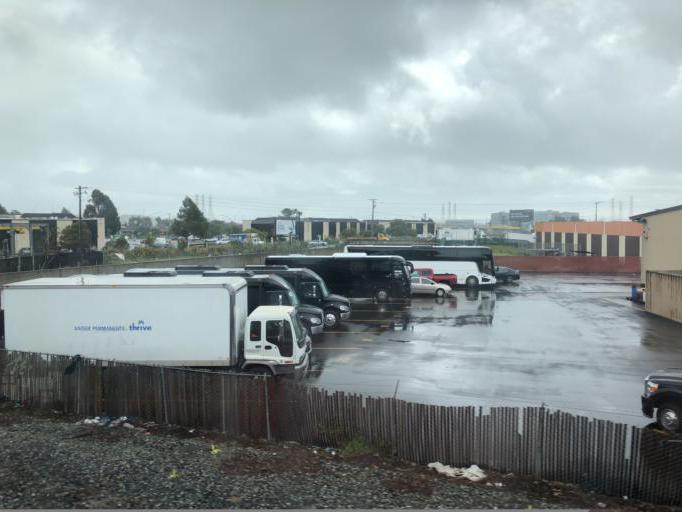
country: US
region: California
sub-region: San Mateo County
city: South San Francisco
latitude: 37.6491
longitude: -122.4108
